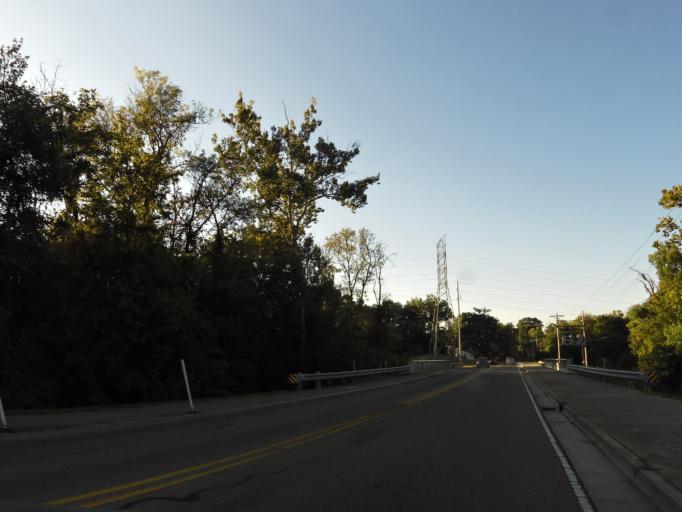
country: US
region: Tennessee
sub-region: Blount County
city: Alcoa
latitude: 35.7918
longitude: -83.9706
